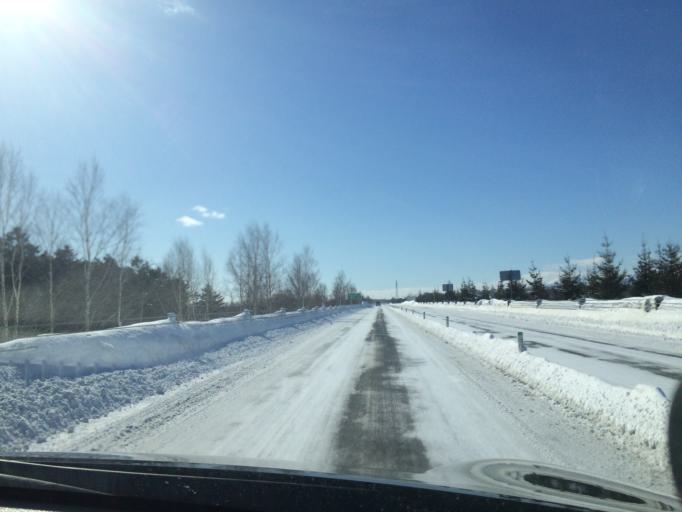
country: JP
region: Hokkaido
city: Chitose
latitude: 42.8713
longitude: 141.6135
